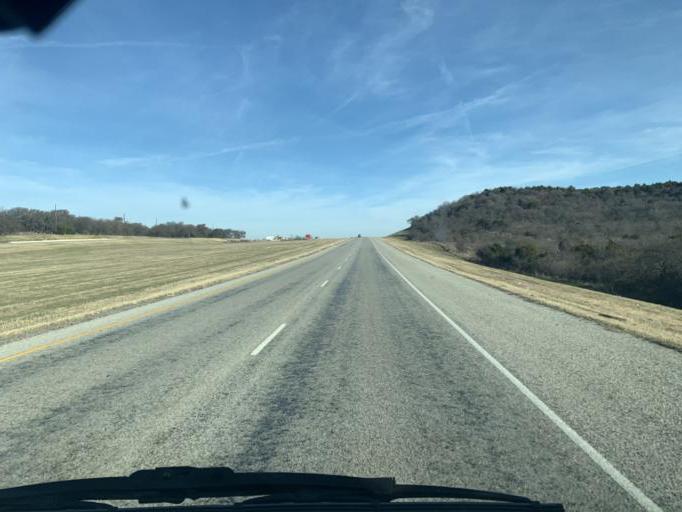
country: US
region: Texas
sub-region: Dallas County
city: Cedar Hill
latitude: 32.6265
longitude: -96.9753
